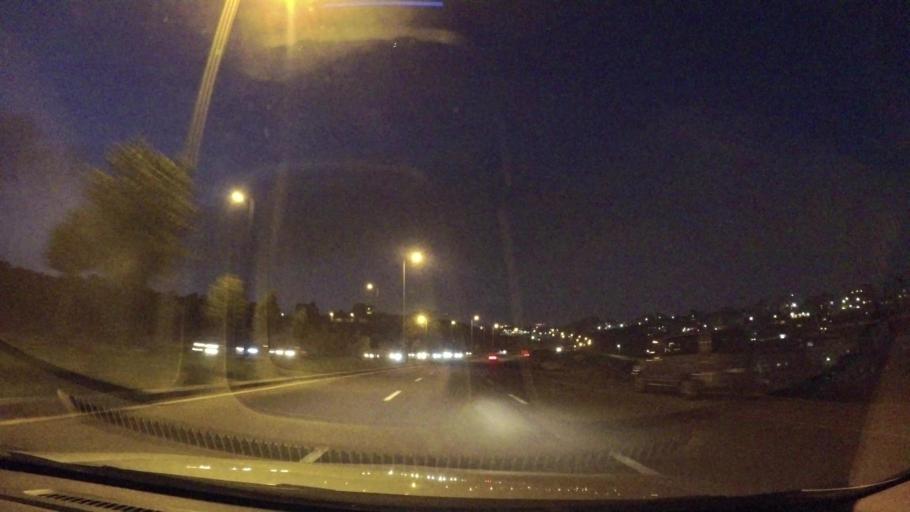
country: JO
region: Amman
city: Al Bunayyat ash Shamaliyah
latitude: 31.9144
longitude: 35.8793
